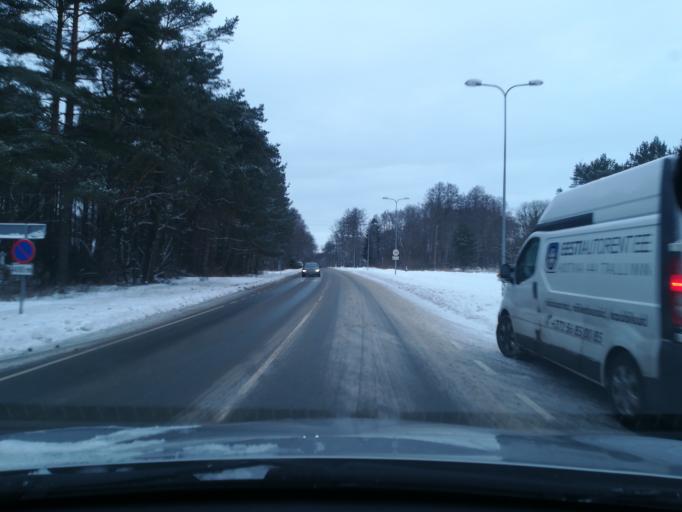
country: EE
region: Harju
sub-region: Keila linn
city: Keila
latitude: 59.4340
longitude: 24.3678
